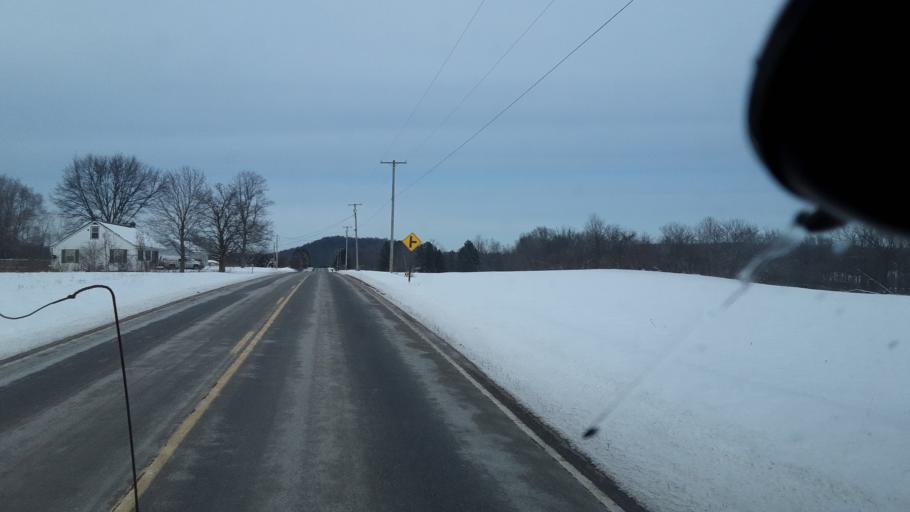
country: US
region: New York
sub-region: Wayne County
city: Newark
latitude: 43.0830
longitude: -77.0576
